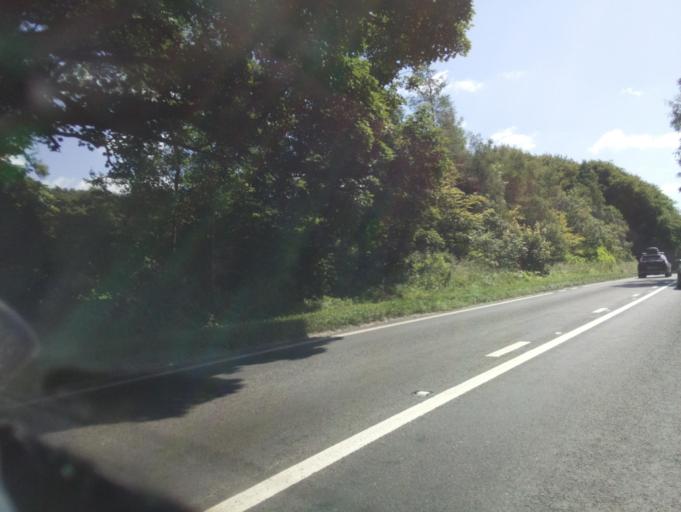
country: GB
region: England
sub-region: Derbyshire
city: Buxton
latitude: 53.2350
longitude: -1.8872
